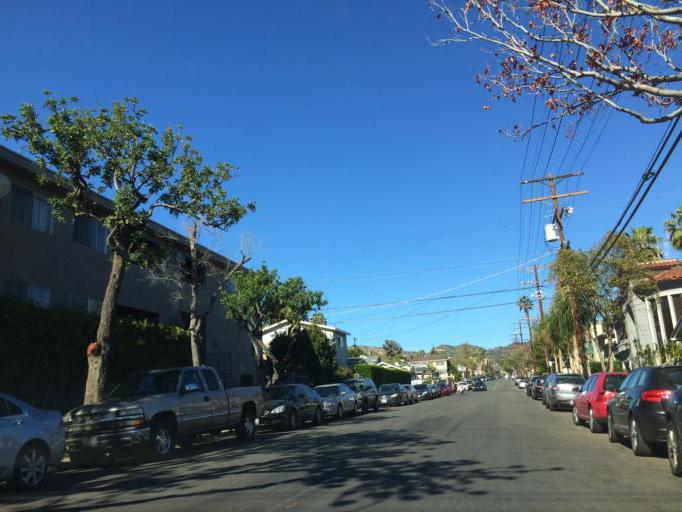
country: US
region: California
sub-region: Los Angeles County
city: Silver Lake
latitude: 34.1019
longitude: -118.2852
